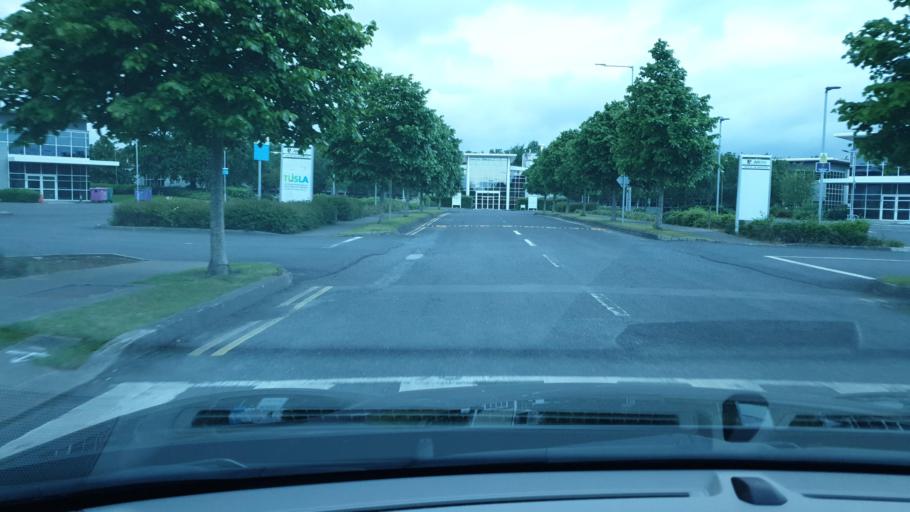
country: IE
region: Leinster
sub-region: Fingal County
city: Swords
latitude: 53.4500
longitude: -6.2183
